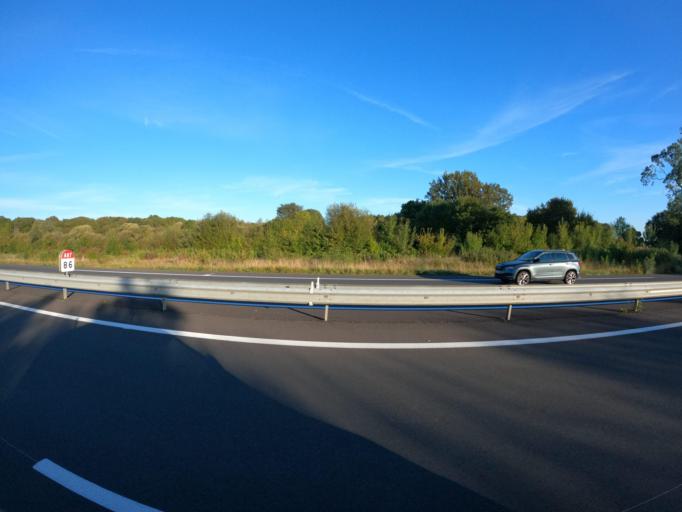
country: FR
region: Pays de la Loire
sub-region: Departement de la Vendee
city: Saint-Fulgent
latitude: 46.8485
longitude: -1.1466
